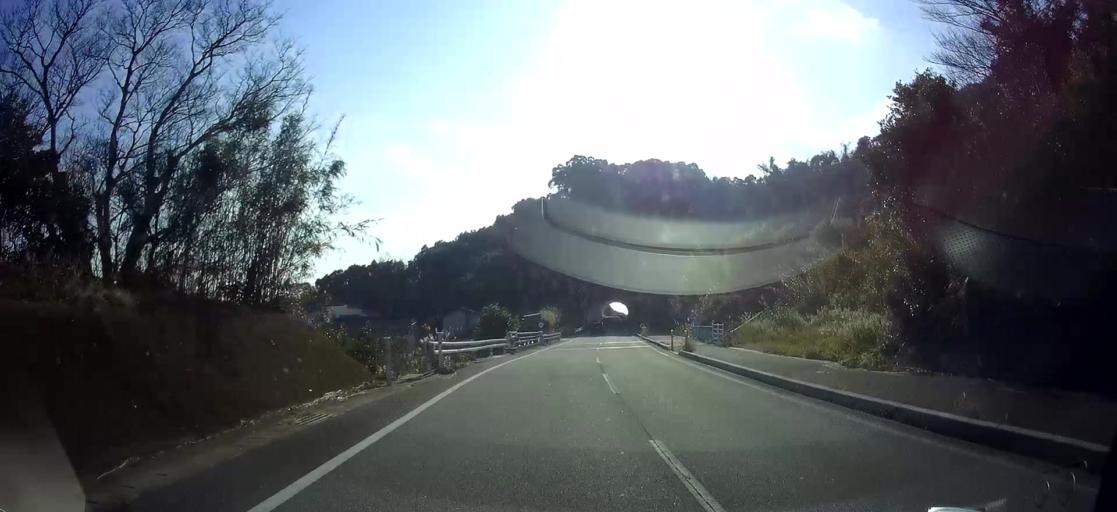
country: JP
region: Kumamoto
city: Minamata
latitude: 32.3987
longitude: 130.3985
